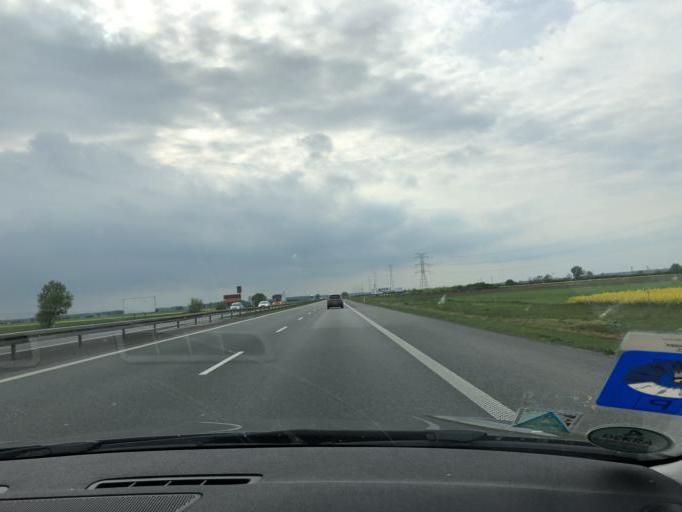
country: PL
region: Opole Voivodeship
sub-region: Powiat brzeski
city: Lewin Brzeski
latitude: 50.7105
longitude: 17.5955
